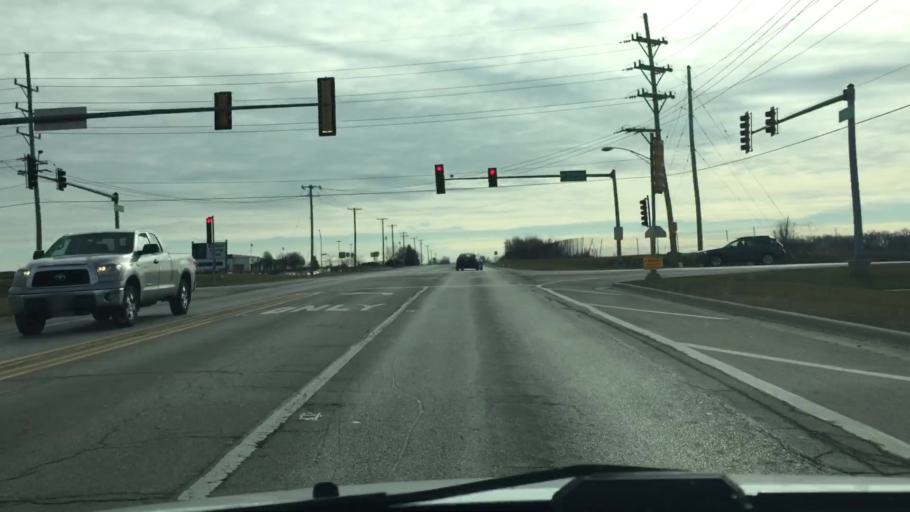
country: US
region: Illinois
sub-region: Kane County
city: South Elgin
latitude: 41.9939
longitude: -88.2681
